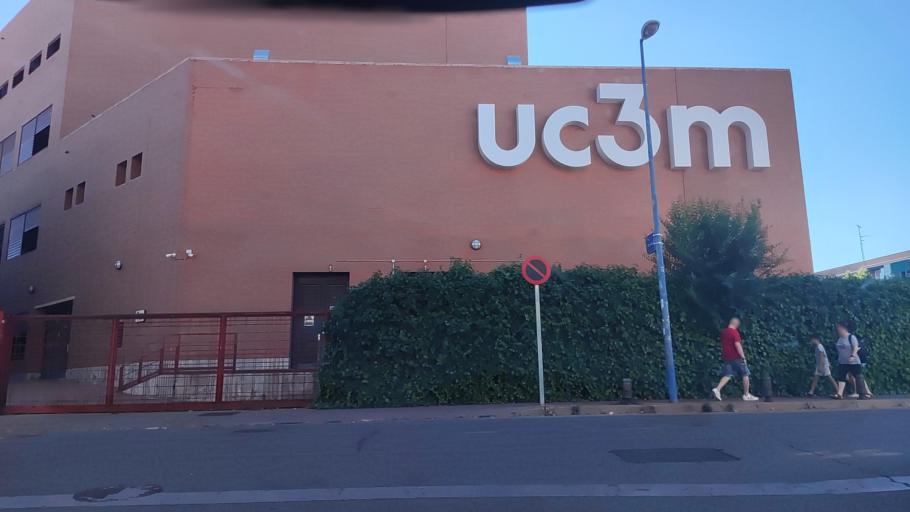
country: ES
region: Madrid
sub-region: Provincia de Madrid
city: Leganes
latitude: 40.3343
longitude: -3.7648
